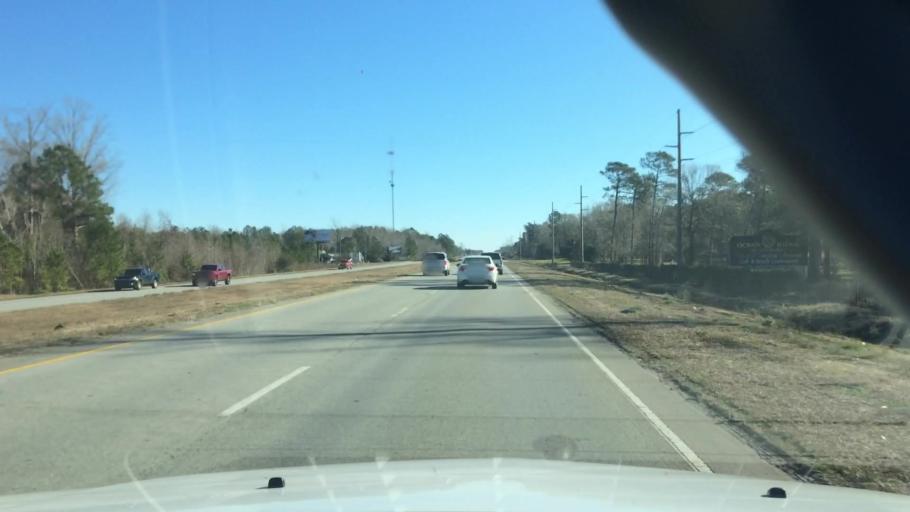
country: US
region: North Carolina
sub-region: Brunswick County
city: Sunset Beach
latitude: 33.9471
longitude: -78.4973
